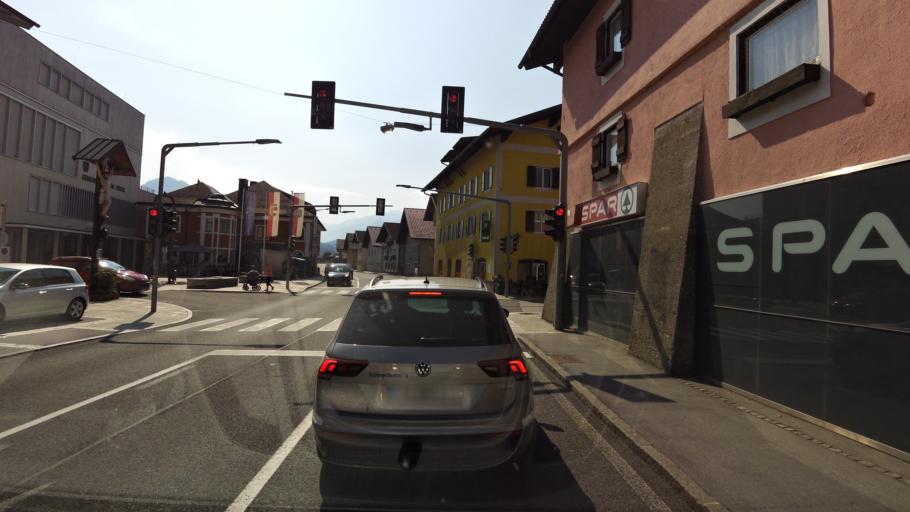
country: AT
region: Salzburg
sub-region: Politischer Bezirk Hallein
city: Kuchl
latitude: 47.6269
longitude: 13.1449
